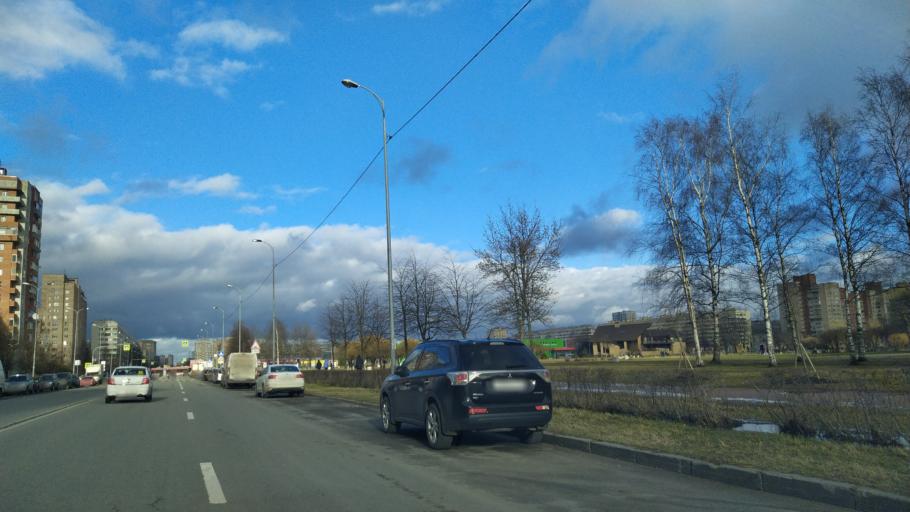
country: RU
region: St.-Petersburg
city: Grazhdanka
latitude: 60.0398
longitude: 30.3844
